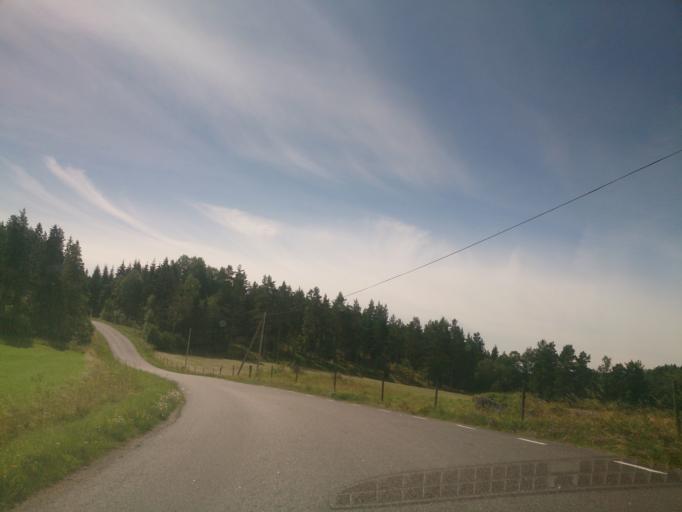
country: SE
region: OEstergoetland
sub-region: Valdemarsviks Kommun
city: Valdemarsvik
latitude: 58.3316
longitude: 16.6378
